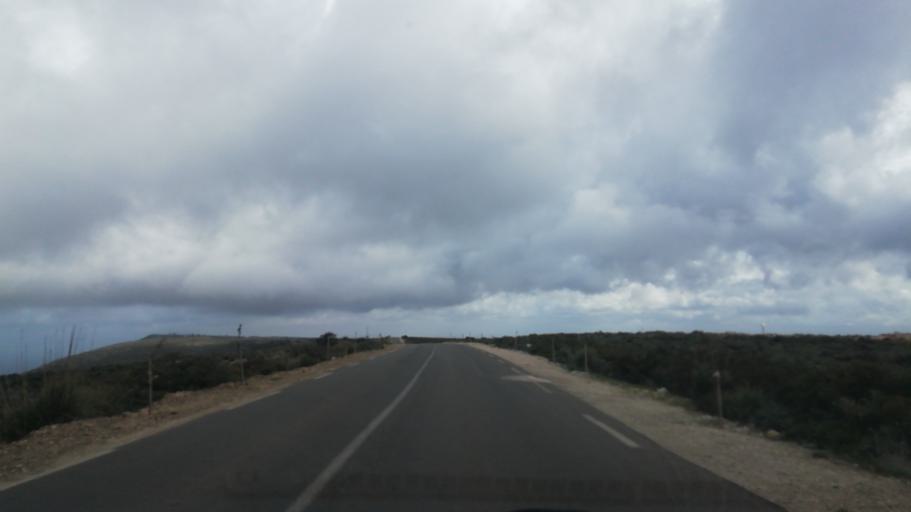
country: DZ
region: Oran
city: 'Ain el Turk
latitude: 35.6994
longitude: -0.7604
